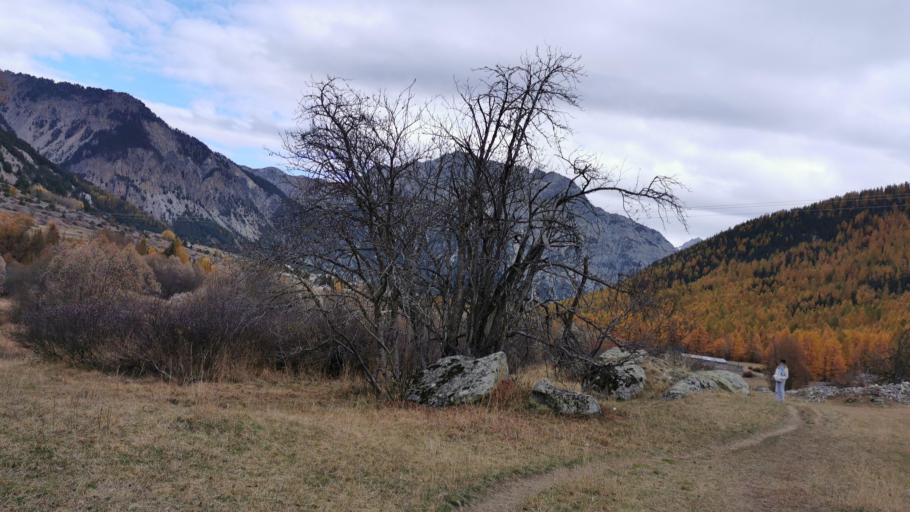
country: FR
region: Provence-Alpes-Cote d'Azur
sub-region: Departement des Hautes-Alpes
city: Villeneuve
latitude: 45.0168
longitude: 6.6143
